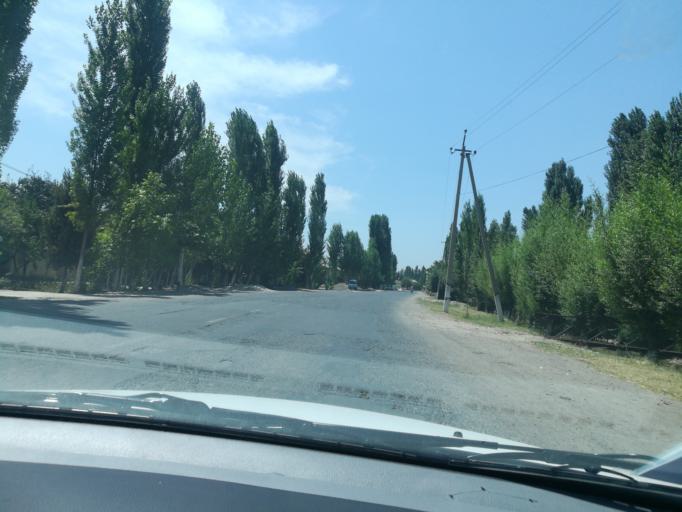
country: UZ
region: Namangan
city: Uchqurghon Shahri
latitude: 41.0753
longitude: 72.0518
